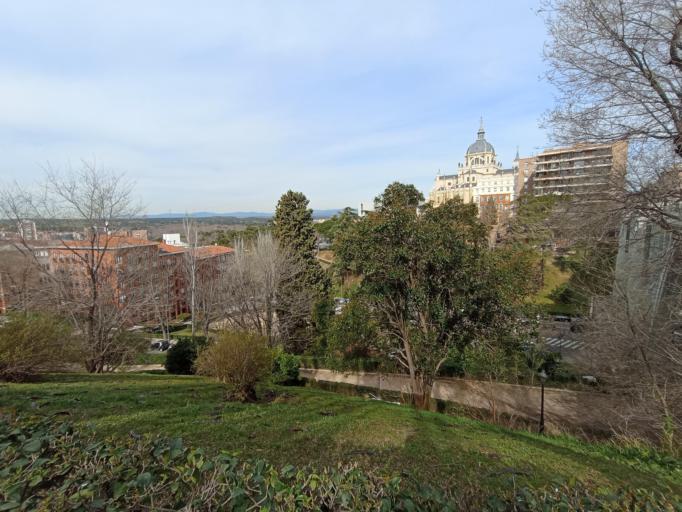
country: ES
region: Madrid
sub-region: Provincia de Madrid
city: Madrid
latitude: 40.4132
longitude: -3.7139
